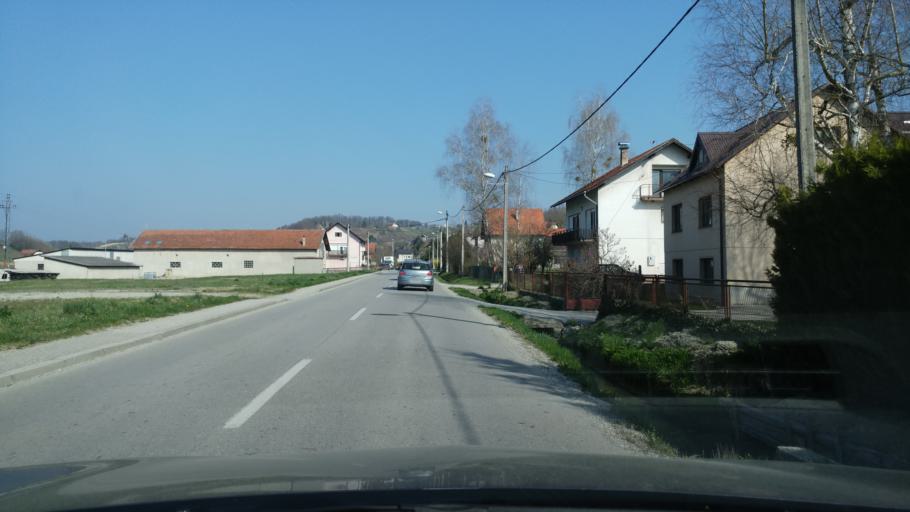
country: HR
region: Zagrebacka
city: Pojatno
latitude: 45.9096
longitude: 15.7803
